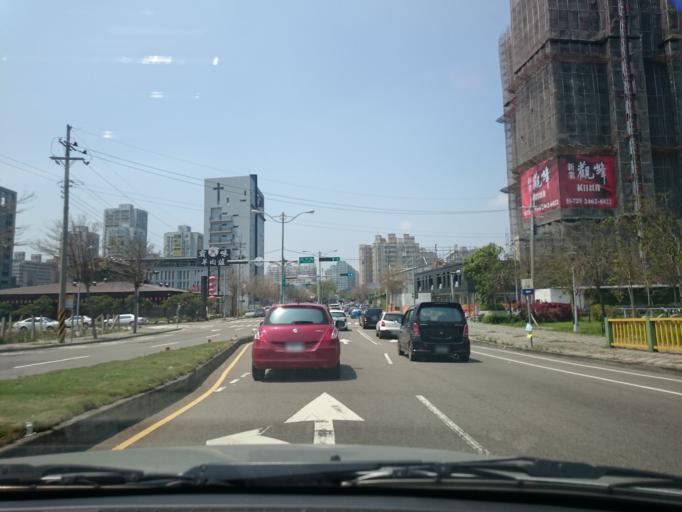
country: TW
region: Taiwan
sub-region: Taichung City
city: Taichung
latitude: 24.1812
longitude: 120.6277
